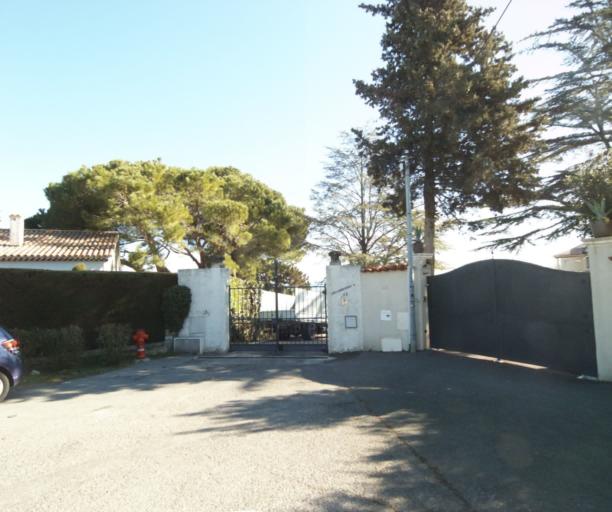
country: FR
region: Provence-Alpes-Cote d'Azur
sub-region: Departement des Alpes-Maritimes
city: Biot
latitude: 43.6126
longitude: 7.0976
